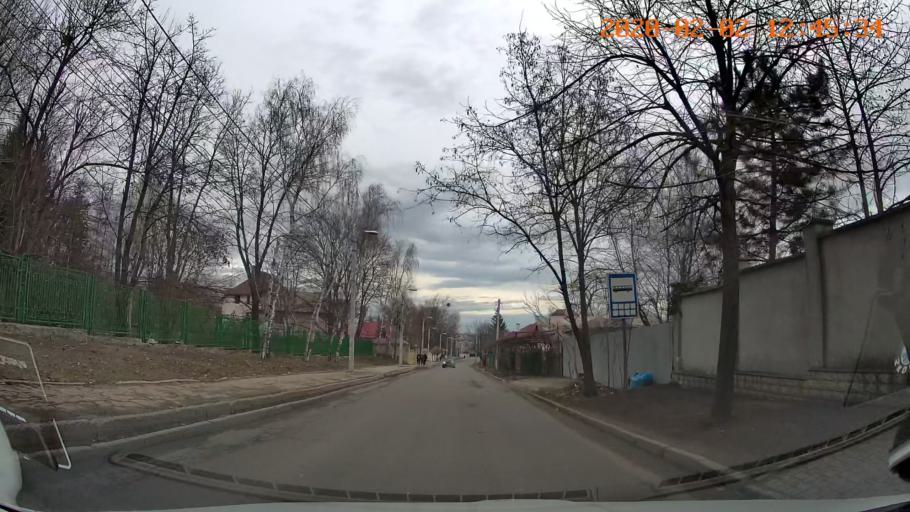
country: MD
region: Chisinau
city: Chisinau
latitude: 47.0057
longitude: 28.8143
